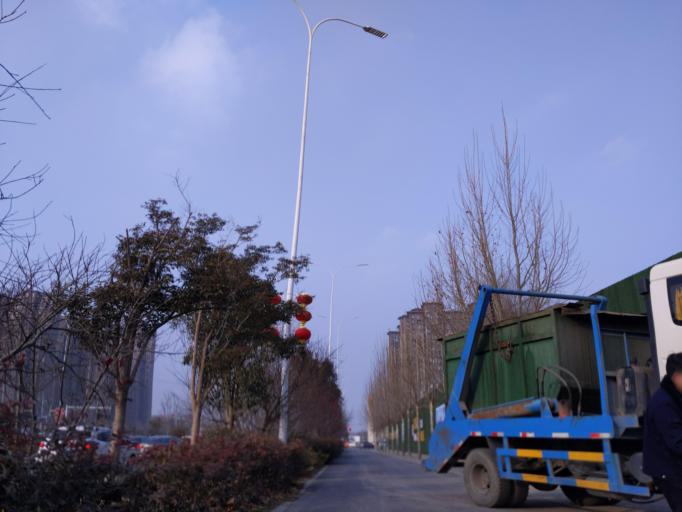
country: CN
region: Henan Sheng
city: Puyang
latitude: 35.8125
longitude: 115.0225
